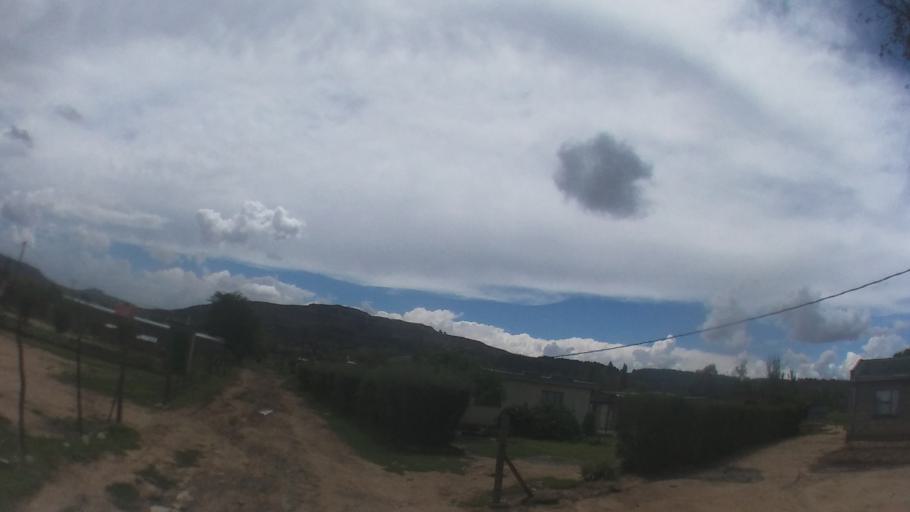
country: LS
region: Maseru
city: Nako
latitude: -29.6193
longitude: 27.5069
